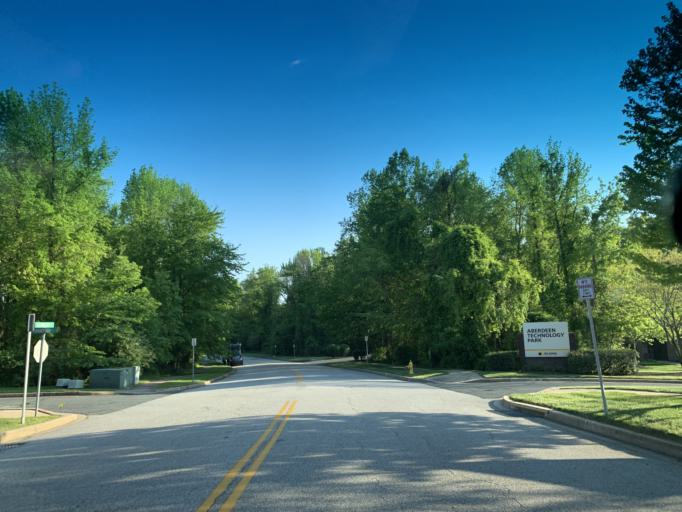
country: US
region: Maryland
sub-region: Harford County
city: Aberdeen
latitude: 39.5287
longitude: -76.1981
